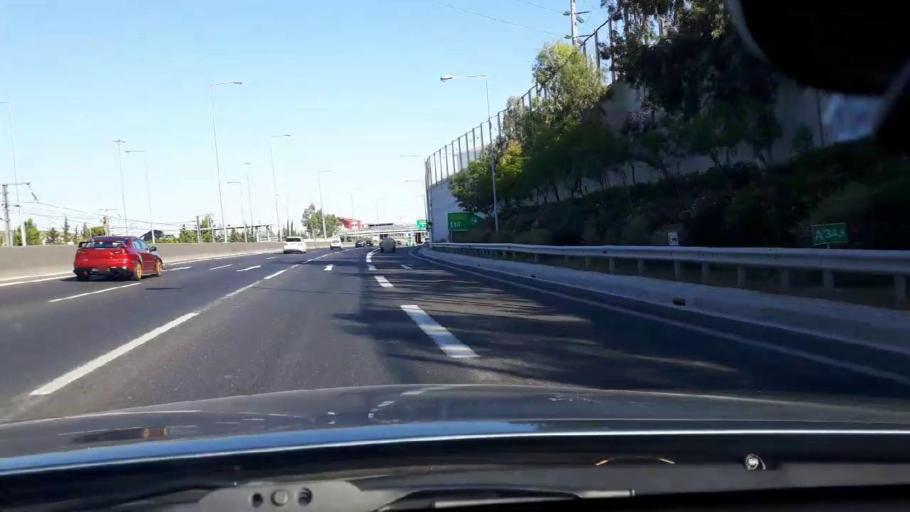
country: GR
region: Attica
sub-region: Nomarchia Anatolikis Attikis
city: Pallini
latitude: 38.0078
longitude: 23.8686
